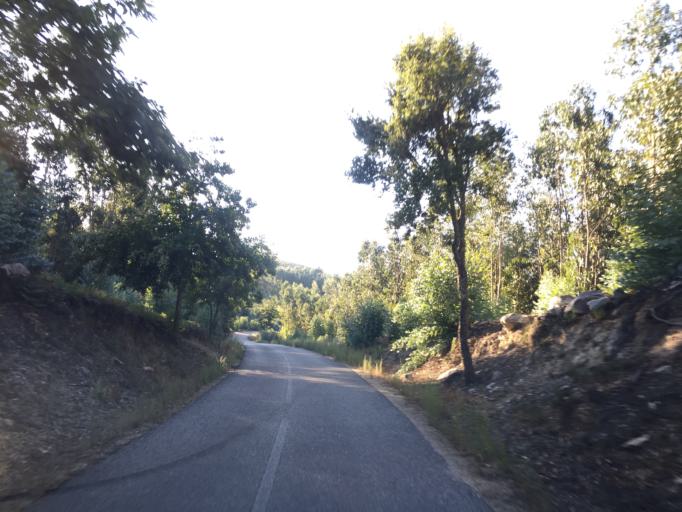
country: PT
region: Portalegre
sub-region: Castelo de Vide
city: Castelo de Vide
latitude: 39.4039
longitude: -7.4558
